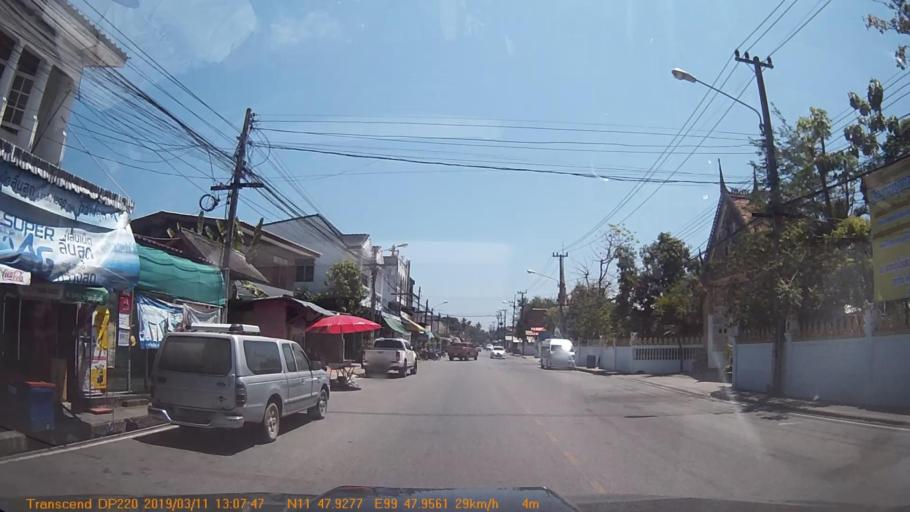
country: TH
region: Prachuap Khiri Khan
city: Prachuap Khiri Khan
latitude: 11.7986
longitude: 99.7993
